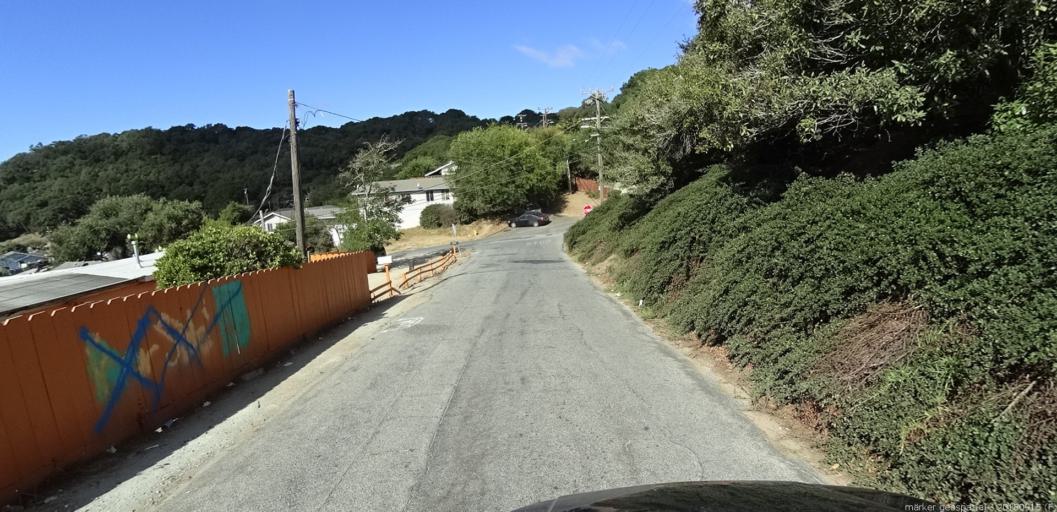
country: US
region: California
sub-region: Monterey County
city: Las Lomas
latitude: 36.8777
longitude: -121.7336
